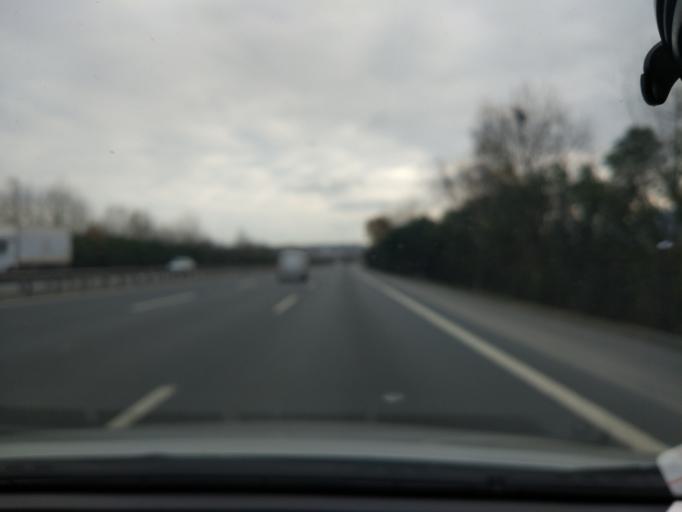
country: TR
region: Kocaeli
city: Derbent
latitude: 40.7250
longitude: 30.0906
